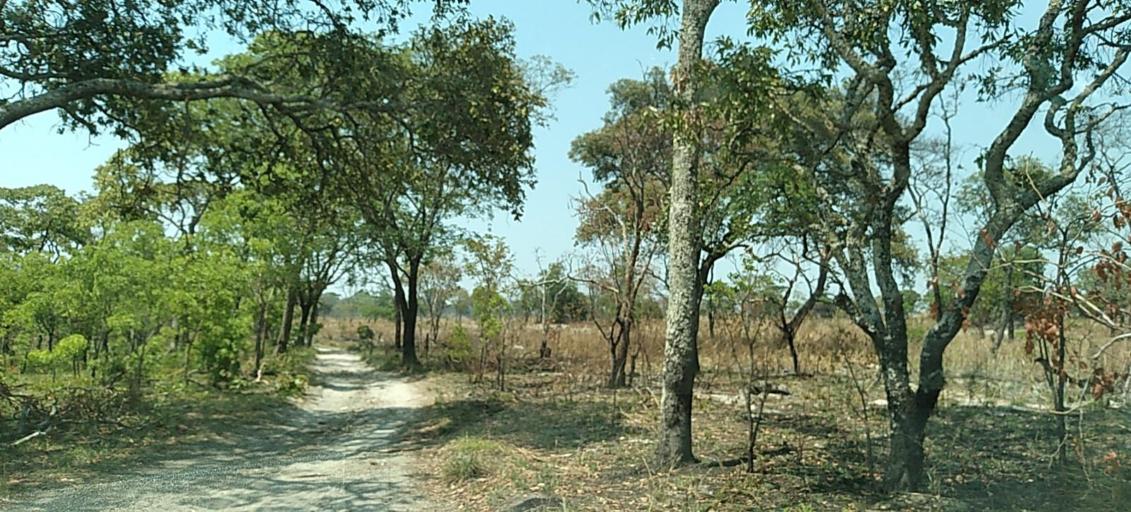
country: ZM
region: Copperbelt
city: Mpongwe
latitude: -13.8532
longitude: 28.0571
